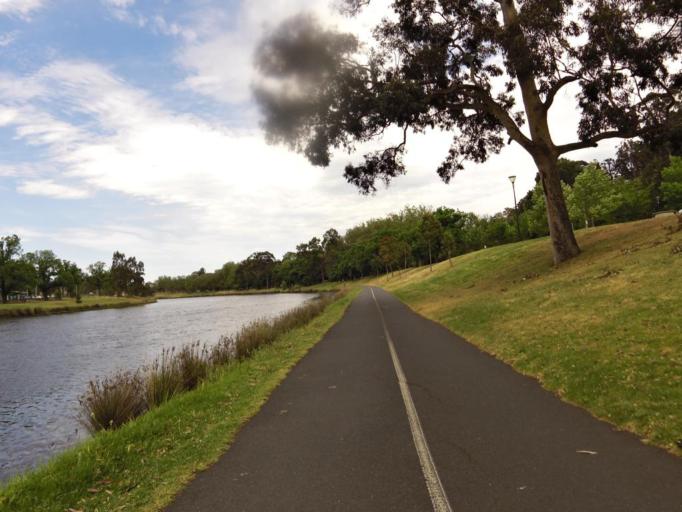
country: AU
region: Victoria
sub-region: Melbourne
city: East Melbourne
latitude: -37.8251
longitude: 144.9786
